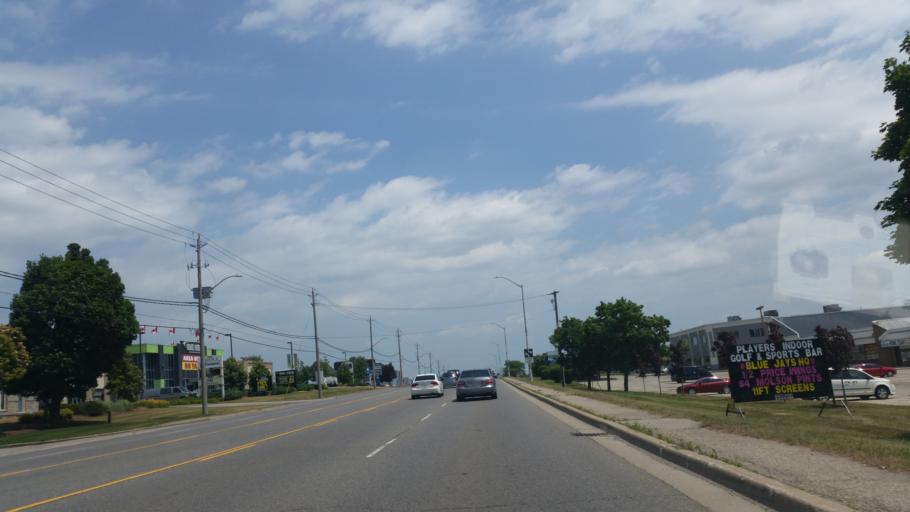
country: CA
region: Ontario
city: Waterloo
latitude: 43.4698
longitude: -80.4467
